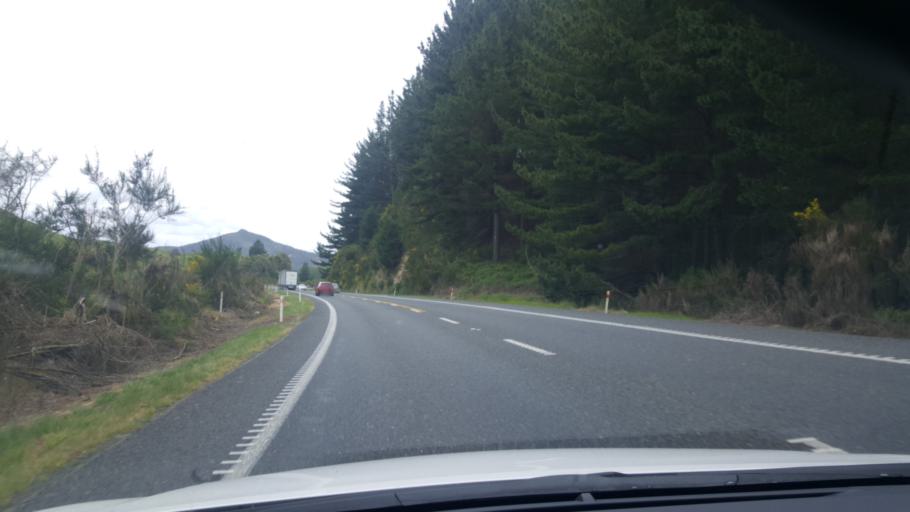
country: NZ
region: Bay of Plenty
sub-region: Rotorua District
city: Rotorua
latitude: -38.2866
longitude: 176.3489
